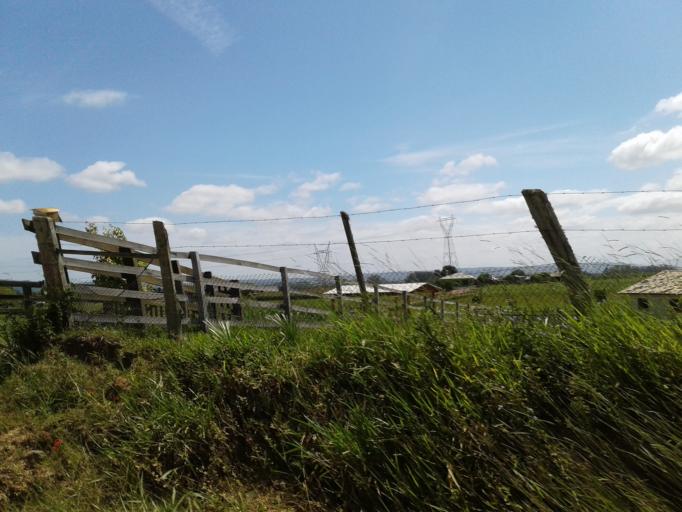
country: BR
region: Rio Grande do Sul
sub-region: Gravatai
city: Gravatai
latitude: -29.8765
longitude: -50.8195
